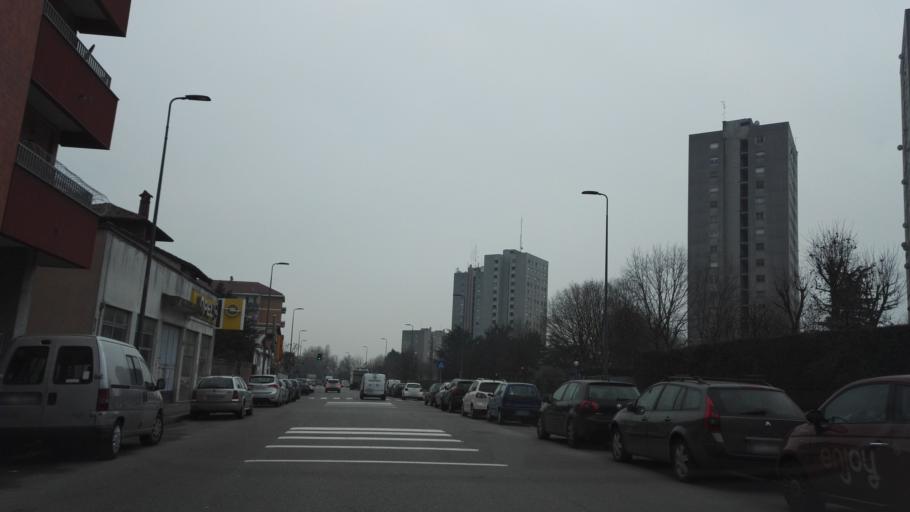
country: IT
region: Lombardy
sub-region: Citta metropolitana di Milano
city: Chiaravalle
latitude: 45.4356
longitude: 9.2179
